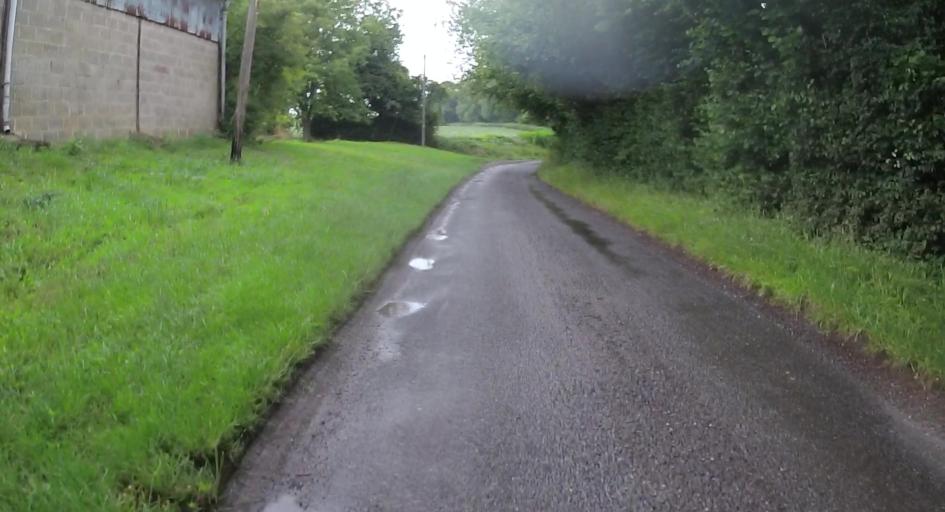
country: GB
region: England
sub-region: Hampshire
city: Long Sutton
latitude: 51.2009
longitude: -0.9147
